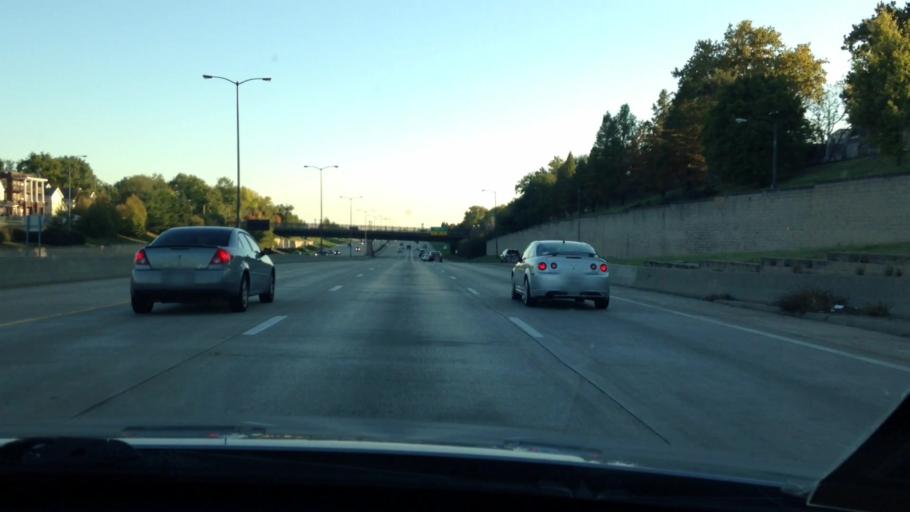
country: US
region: Missouri
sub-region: Jackson County
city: Kansas City
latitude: 39.0656
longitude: -94.5607
